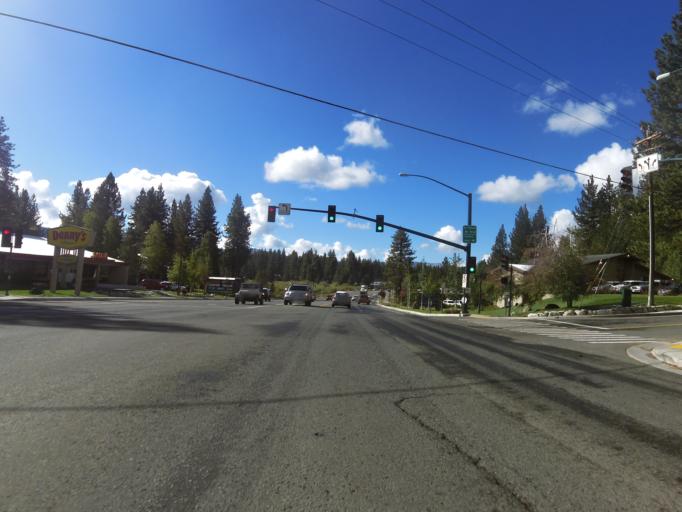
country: US
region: California
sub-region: El Dorado County
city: South Lake Tahoe
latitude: 38.9346
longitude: -119.9777
